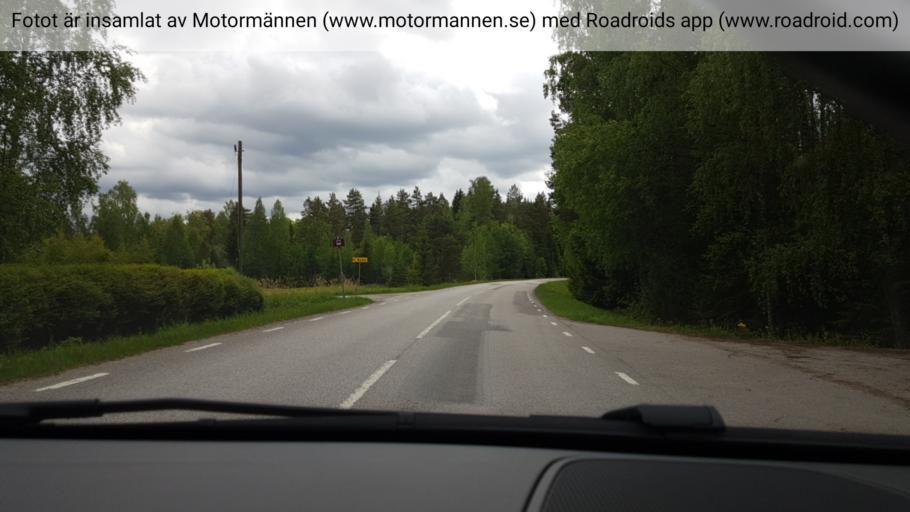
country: SE
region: Uppsala
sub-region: Heby Kommun
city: Tarnsjo
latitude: 60.1098
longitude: 17.0373
